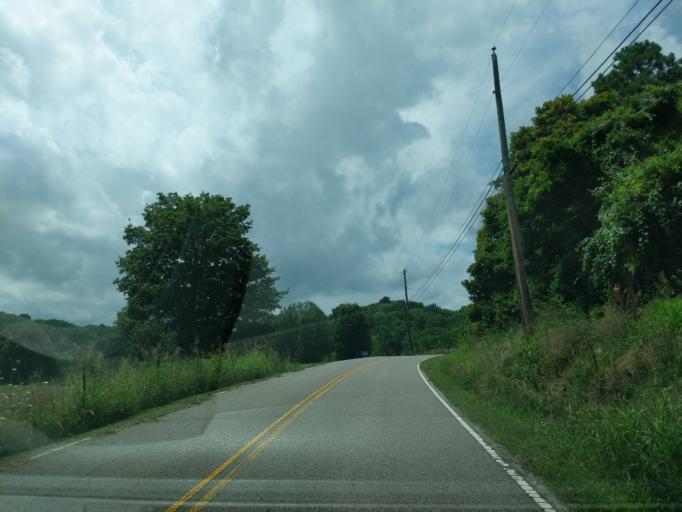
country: US
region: Tennessee
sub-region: Davidson County
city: Goodlettsville
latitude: 36.3144
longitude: -86.7373
